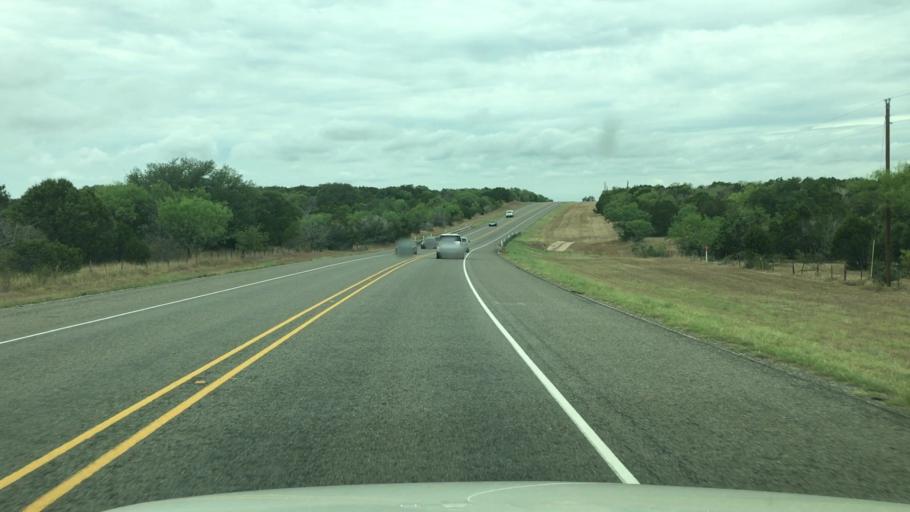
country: US
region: Texas
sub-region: Burnet County
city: Granite Shoals
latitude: 30.5443
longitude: -98.4565
